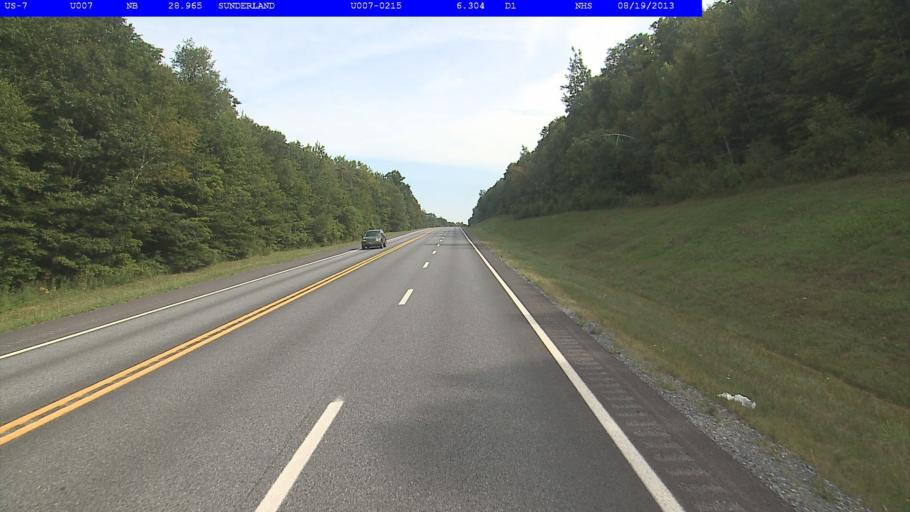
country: US
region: Vermont
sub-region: Bennington County
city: Arlington
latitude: 43.1079
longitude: -73.0902
